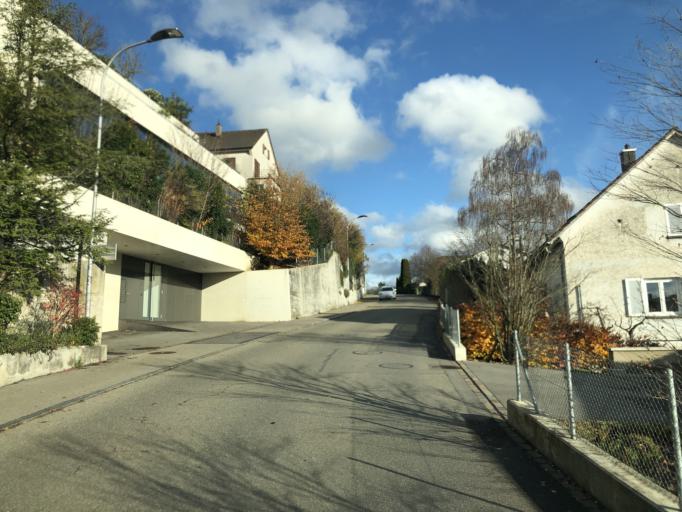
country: CH
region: Aargau
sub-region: Bezirk Baden
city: Wettingen
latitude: 47.4824
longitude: 8.3218
